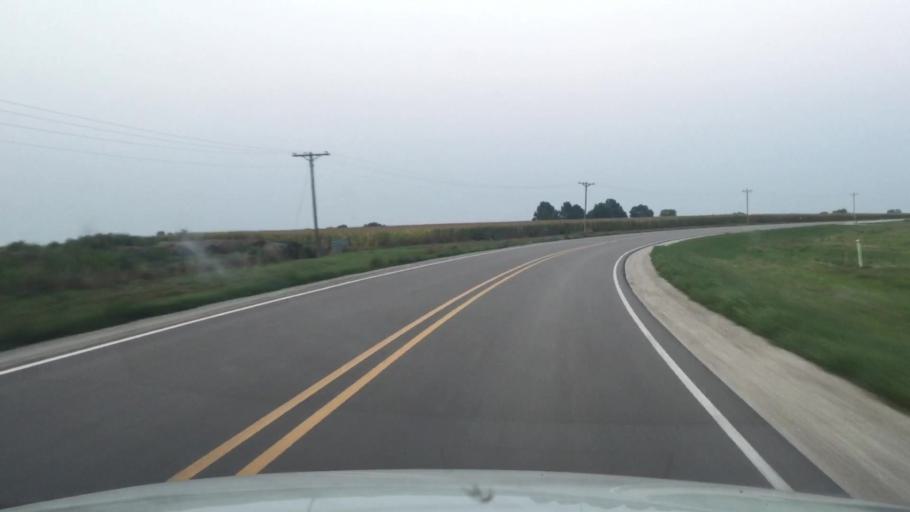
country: US
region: Iowa
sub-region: Warren County
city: Indianola
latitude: 41.1840
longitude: -93.4475
